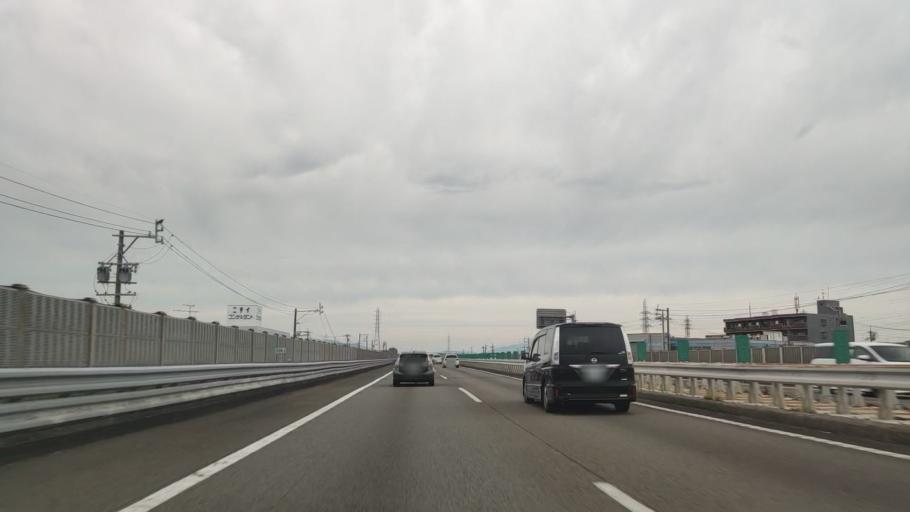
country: JP
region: Aichi
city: Ichinomiya
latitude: 35.2761
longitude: 136.8146
